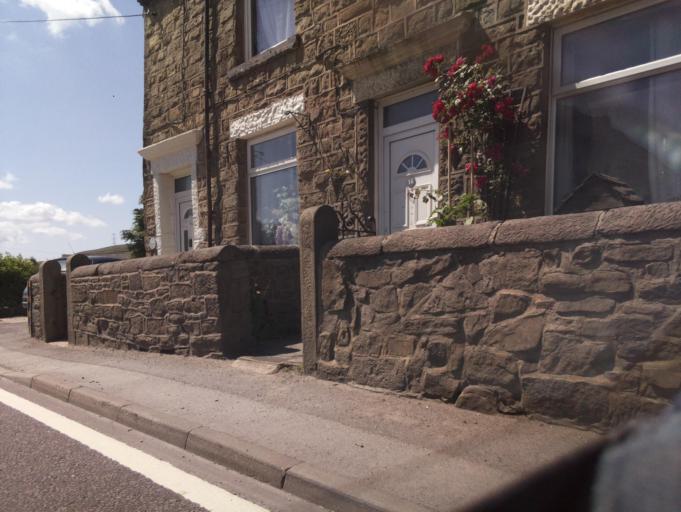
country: GB
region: England
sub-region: Derbyshire
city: Chapel en le Frith
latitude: 53.2976
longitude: -1.8881
